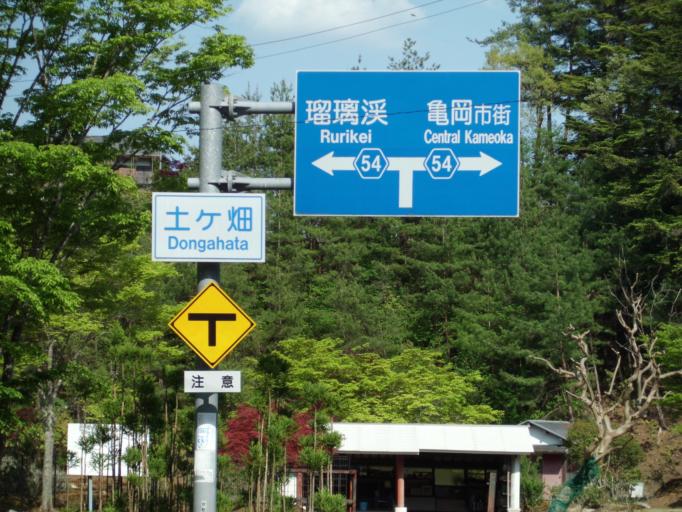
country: JP
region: Hyogo
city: Sasayama
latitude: 35.0275
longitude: 135.3893
